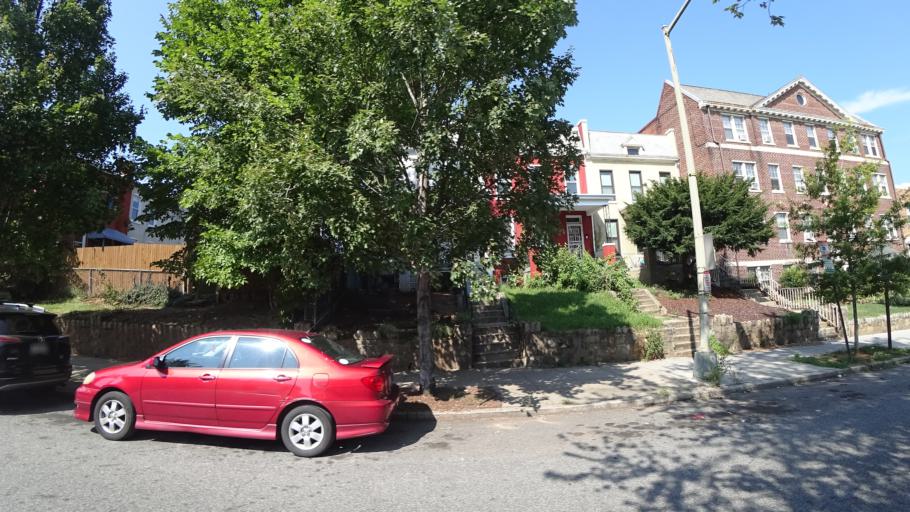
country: US
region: Washington, D.C.
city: Washington, D.C.
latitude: 38.8965
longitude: -76.9883
